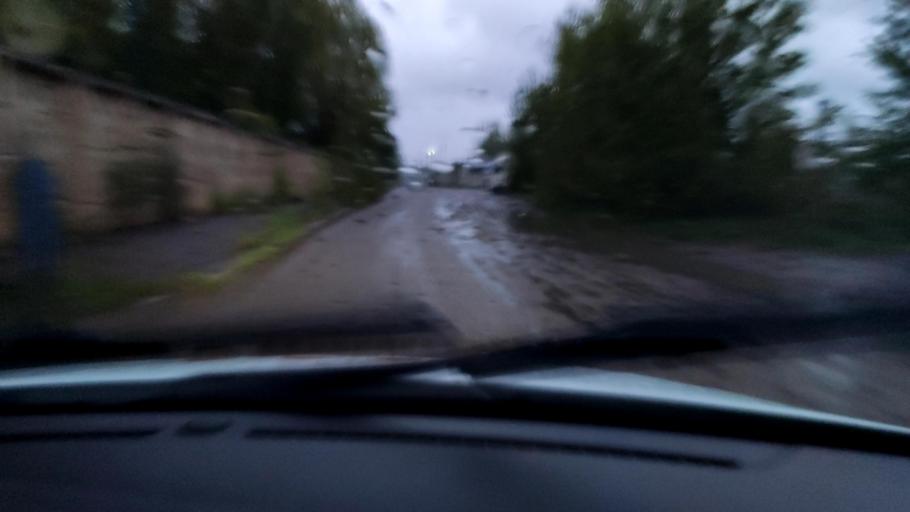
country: RU
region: Tatarstan
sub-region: Gorod Kazan'
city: Kazan
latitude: 55.7199
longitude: 49.1243
